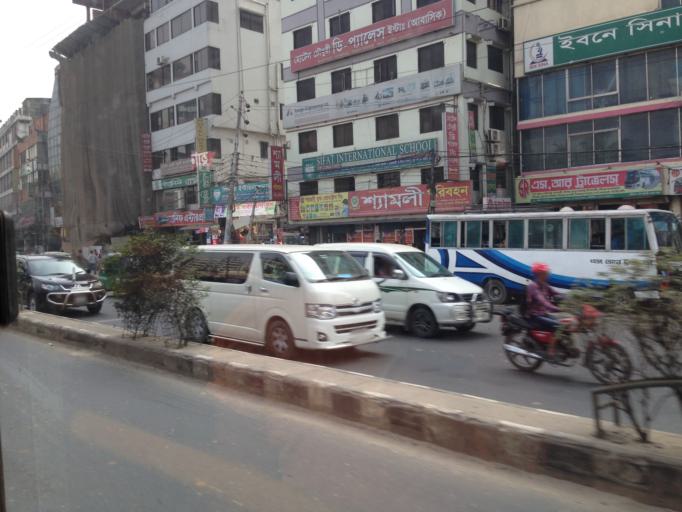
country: BD
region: Dhaka
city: Azimpur
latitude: 23.7785
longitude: 90.3600
